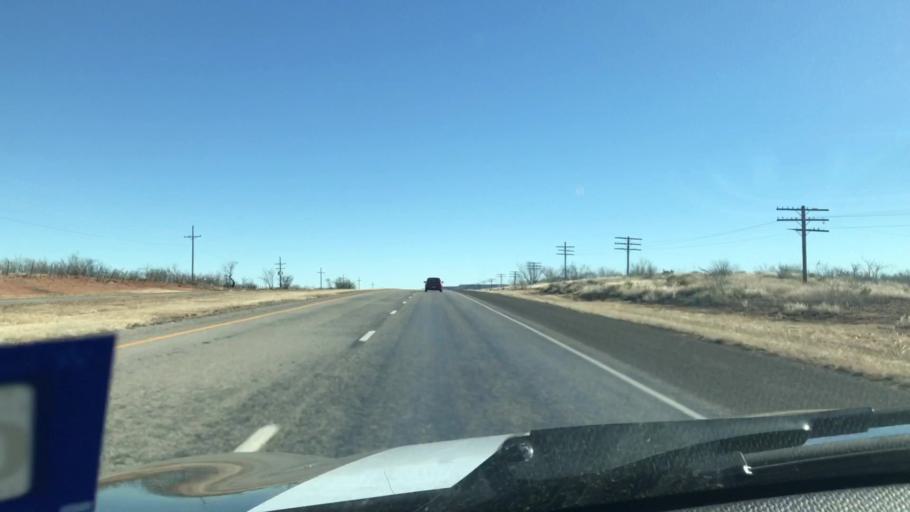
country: US
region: Texas
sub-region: Garza County
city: Post
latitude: 33.0325
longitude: -101.1917
